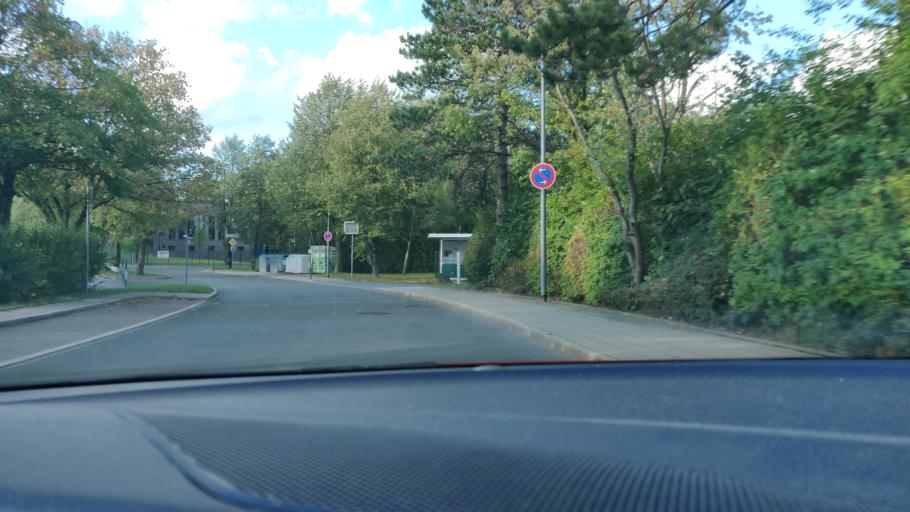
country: DE
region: North Rhine-Westphalia
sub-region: Regierungsbezirk Dusseldorf
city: Velbert
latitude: 51.3287
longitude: 7.0396
